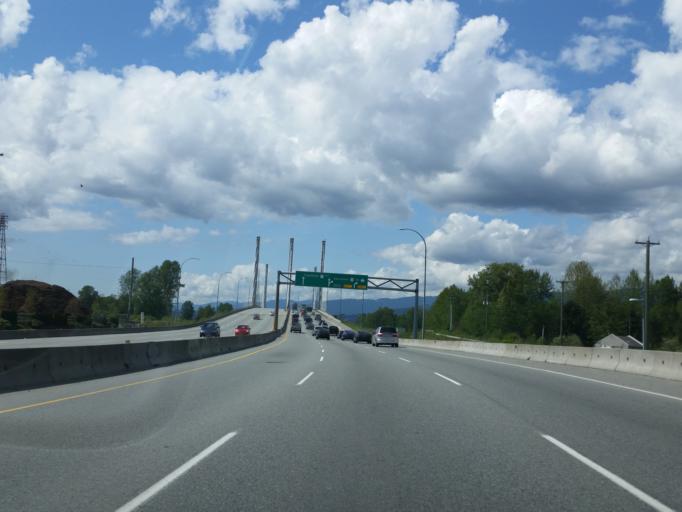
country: CA
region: British Columbia
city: Pitt Meadows
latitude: 49.2453
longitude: -122.7230
